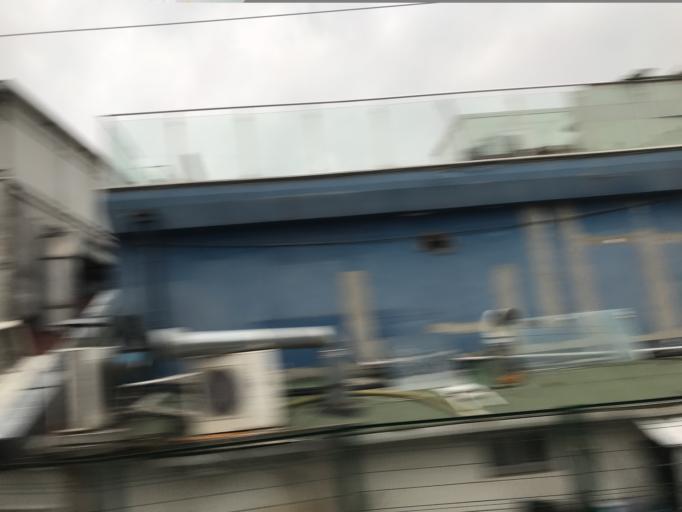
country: TR
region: Istanbul
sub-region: Atasehir
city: Atasehir
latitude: 40.9406
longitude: 29.1121
